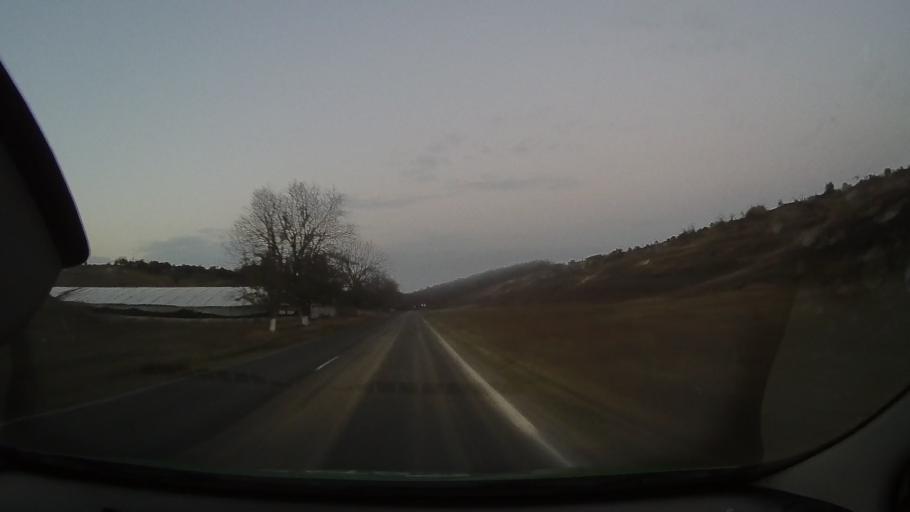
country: RO
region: Constanta
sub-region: Comuna Baneasa
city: Baneasa
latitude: 44.0747
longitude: 27.7372
